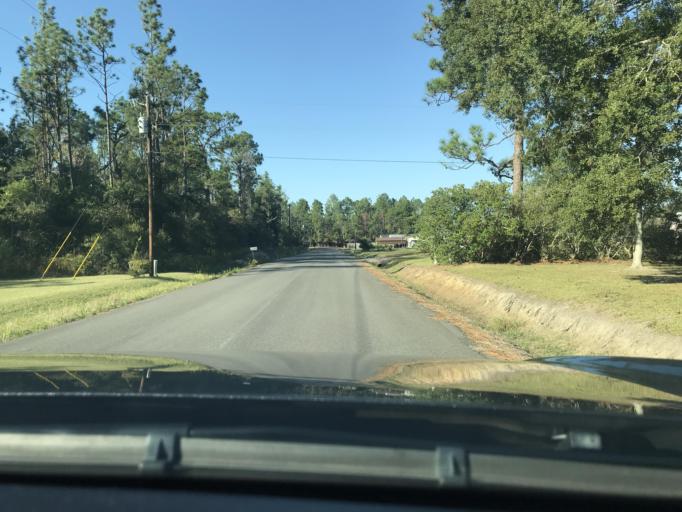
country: US
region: Louisiana
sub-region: Calcasieu Parish
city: Moss Bluff
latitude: 30.3205
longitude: -93.2688
